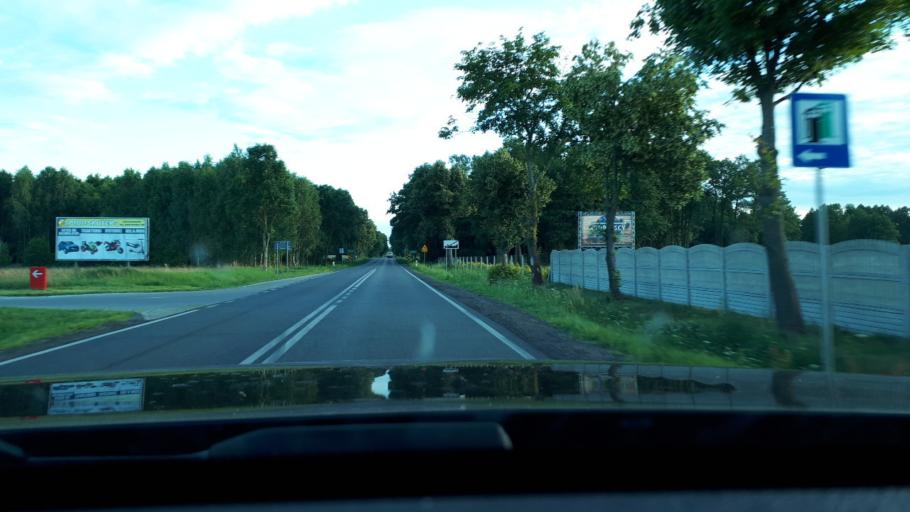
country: PL
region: Masovian Voivodeship
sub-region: Powiat ciechanowski
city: Ojrzen
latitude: 52.7601
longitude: 20.5406
